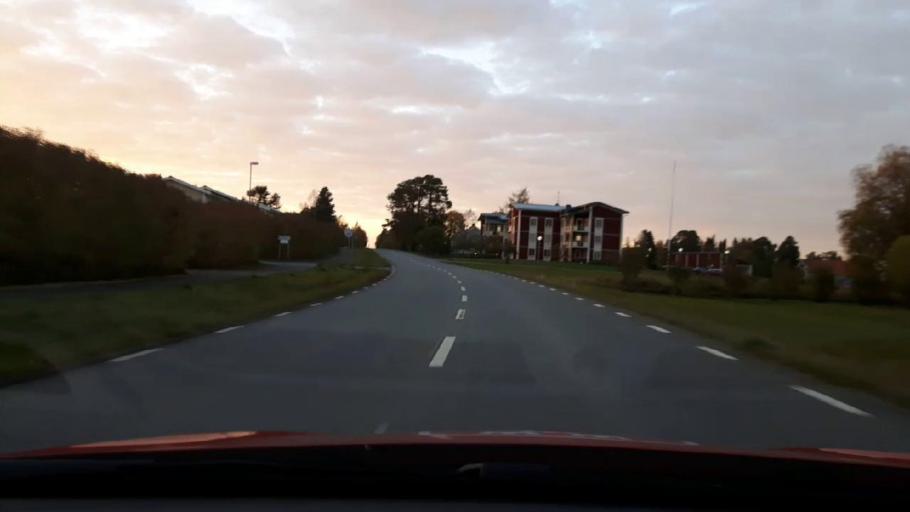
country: SE
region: Jaemtland
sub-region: OEstersunds Kommun
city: Ostersund
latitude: 63.2452
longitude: 14.5725
